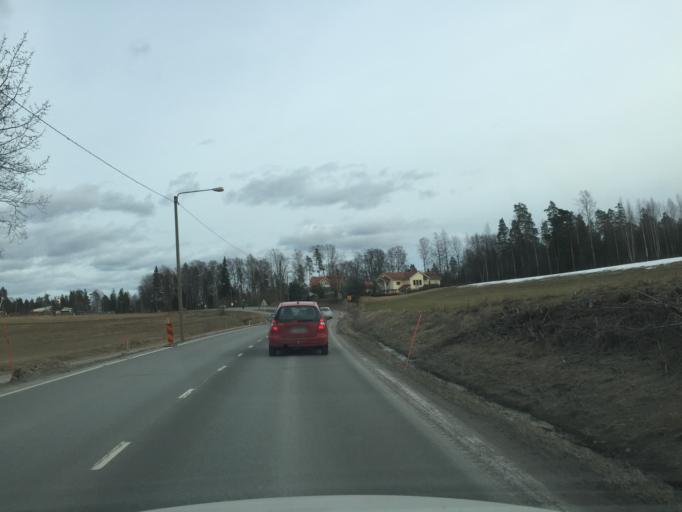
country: FI
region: Uusimaa
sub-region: Helsinki
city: Teekkarikylae
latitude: 60.2873
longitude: 24.8932
